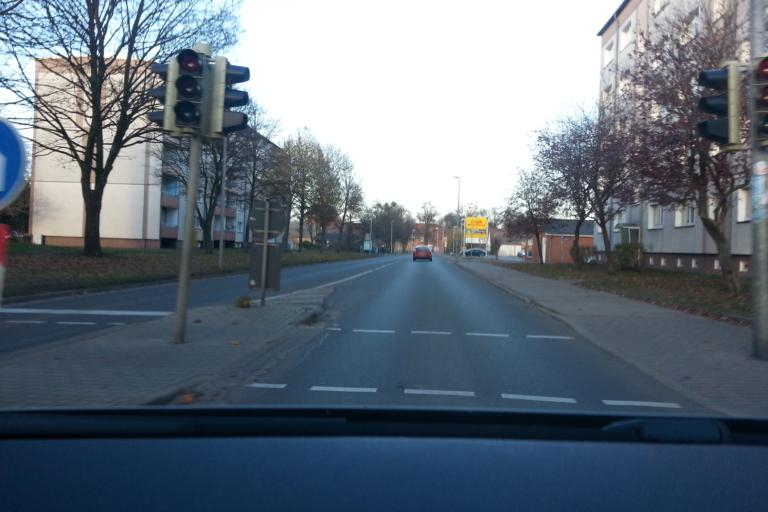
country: DE
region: Mecklenburg-Vorpommern
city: Ferdinandshof
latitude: 53.6619
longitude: 13.8863
